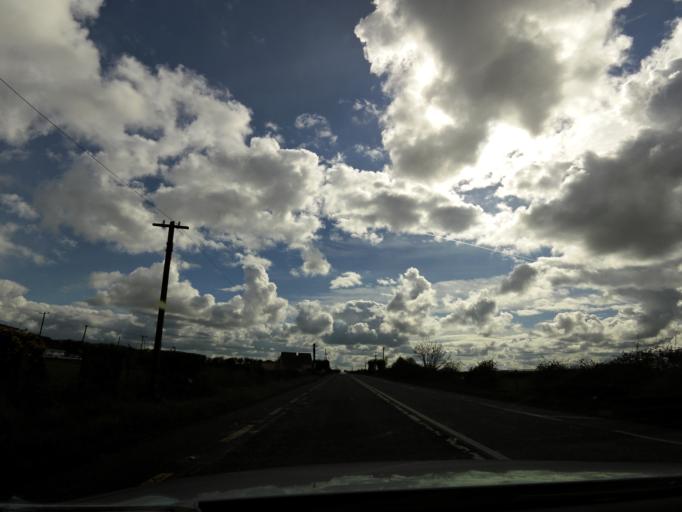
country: IE
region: Leinster
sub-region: Laois
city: Rathdowney
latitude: 52.7993
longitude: -7.5067
